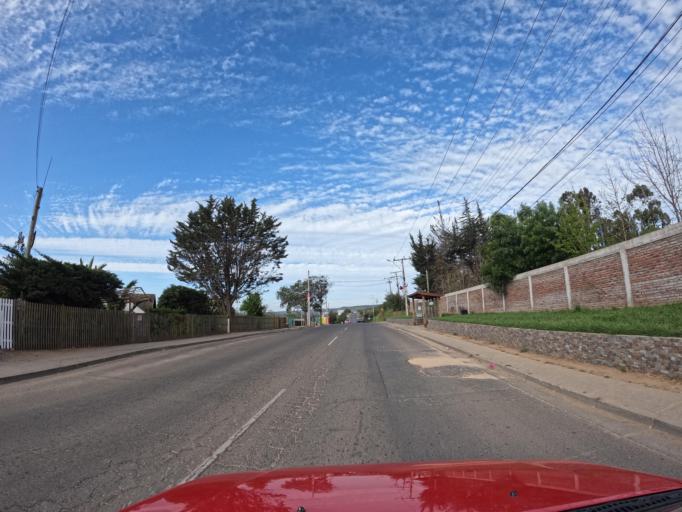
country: CL
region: Valparaiso
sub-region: San Antonio Province
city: San Antonio
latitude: -34.1122
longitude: -71.7232
